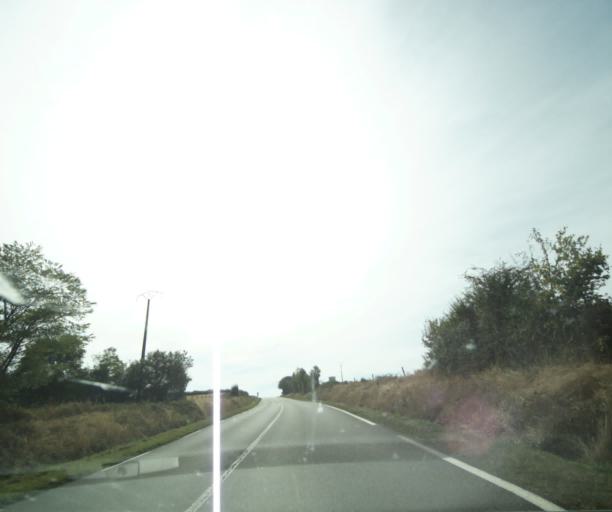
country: FR
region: Auvergne
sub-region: Departement de l'Allier
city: Le Donjon
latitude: 46.3091
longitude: 3.7712
